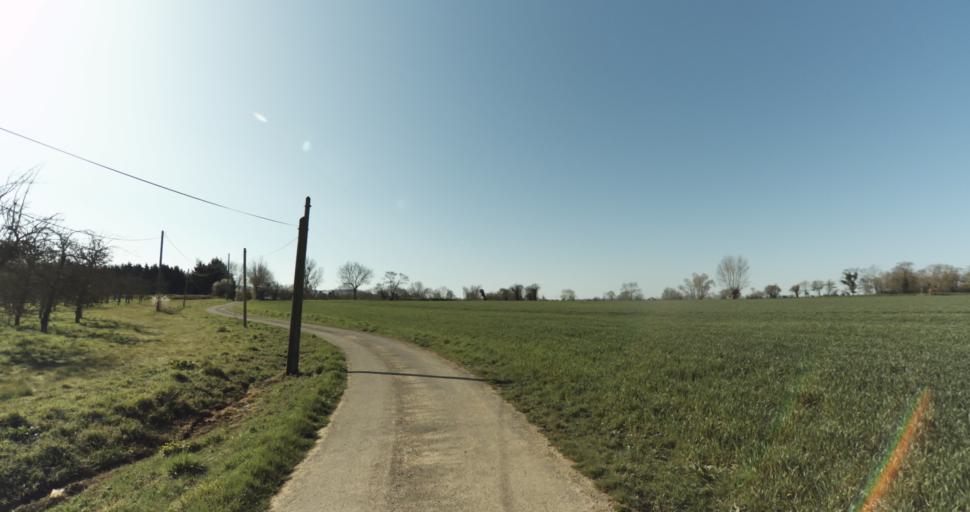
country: FR
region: Lower Normandy
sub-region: Departement du Calvados
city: Saint-Pierre-sur-Dives
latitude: 48.9467
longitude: 0.0278
